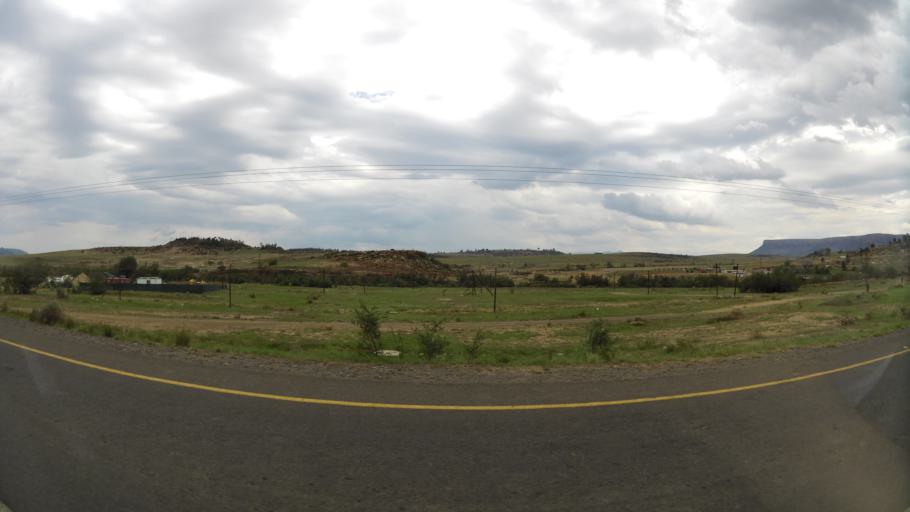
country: LS
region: Maseru
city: Maseru
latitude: -29.3977
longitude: 27.4738
